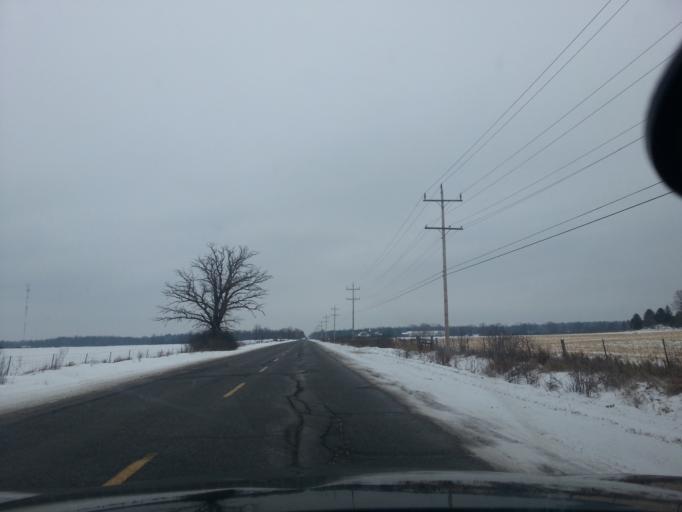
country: CA
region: Ontario
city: Arnprior
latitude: 45.4105
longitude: -76.1584
